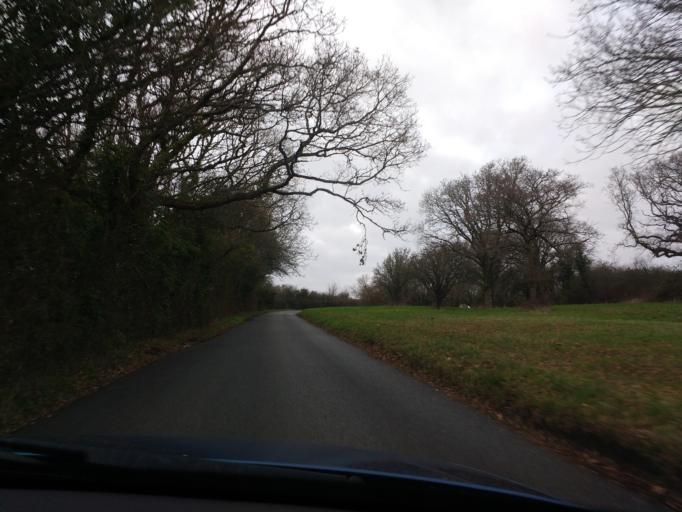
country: GB
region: England
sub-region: Isle of Wight
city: Shalfleet
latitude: 50.7117
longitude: -1.4017
